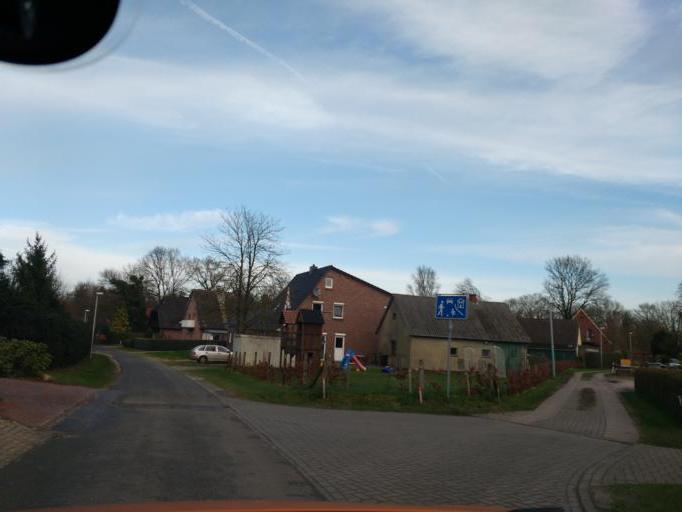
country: DE
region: Lower Saxony
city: Hude
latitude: 53.0947
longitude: 8.4566
